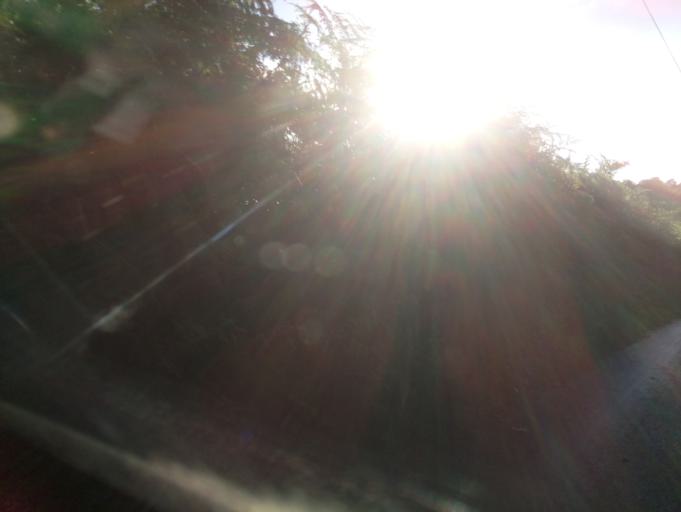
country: GB
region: England
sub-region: Devon
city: Totnes
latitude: 50.3474
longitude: -3.7034
